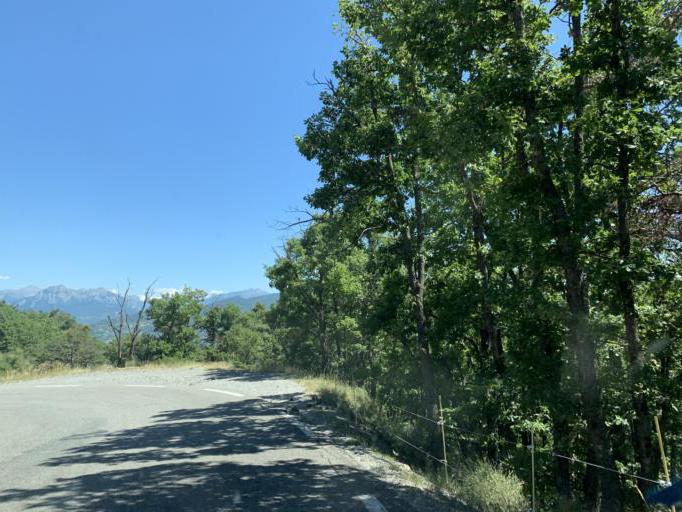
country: FR
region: Provence-Alpes-Cote d'Azur
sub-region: Departement des Hautes-Alpes
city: La Batie-Neuve
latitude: 44.5874
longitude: 6.1590
